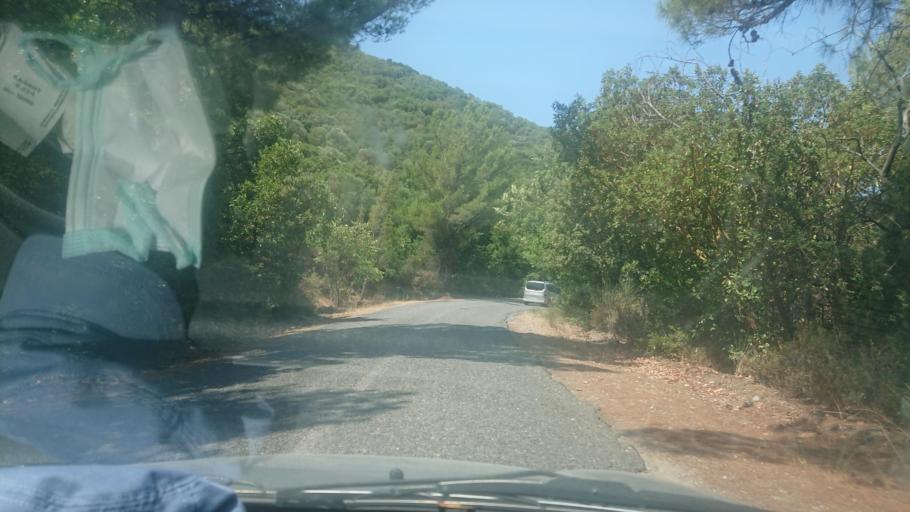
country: TR
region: Aydin
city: Atburgazi
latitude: 37.6971
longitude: 27.1758
